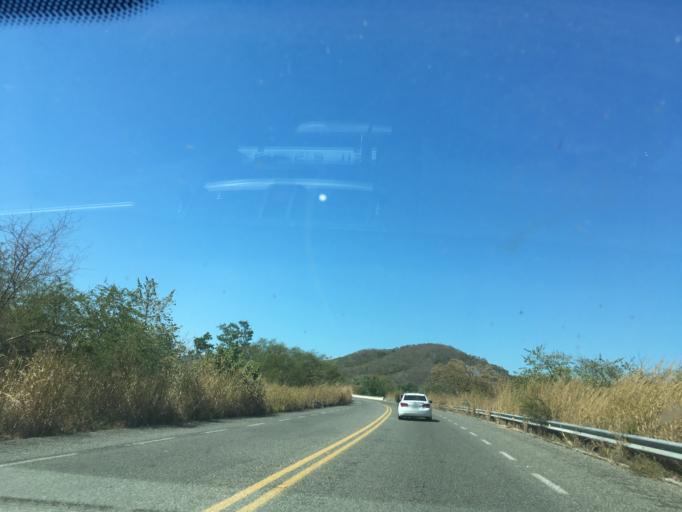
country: MX
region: Guerrero
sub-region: Zihuatanejo de Azueta
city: Pantla
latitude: 17.7525
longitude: -101.6368
